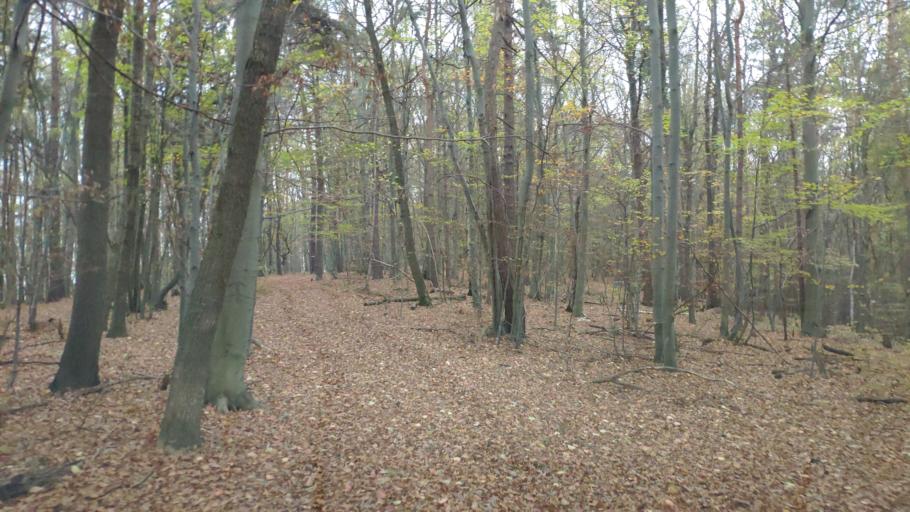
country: SK
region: Presovsky
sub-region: Okres Presov
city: Presov
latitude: 48.9413
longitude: 21.1020
